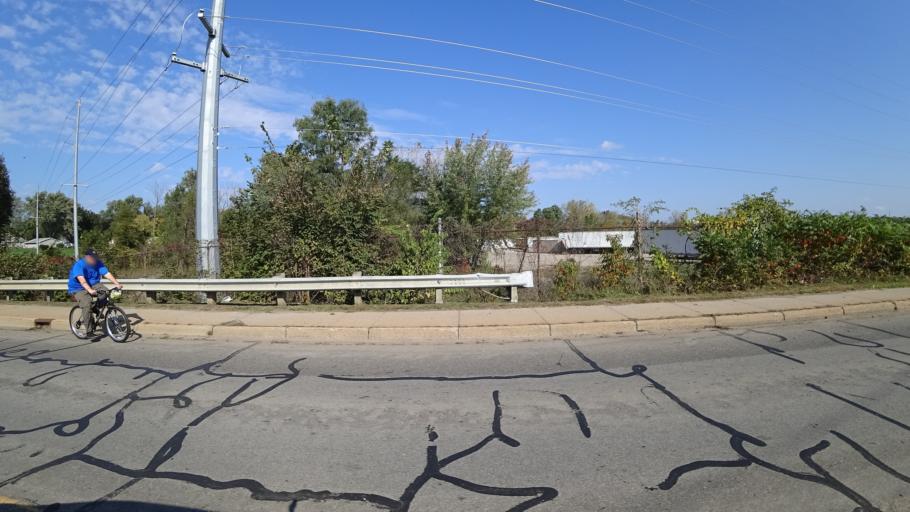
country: US
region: Michigan
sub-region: Saint Joseph County
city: Three Rivers
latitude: 41.9331
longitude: -85.6351
